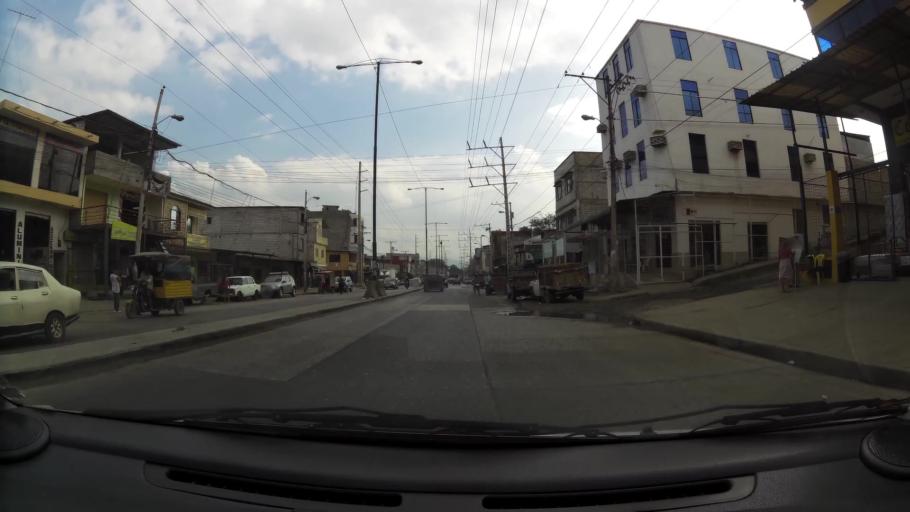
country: EC
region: Guayas
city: Santa Lucia
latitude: -2.1191
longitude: -79.9670
